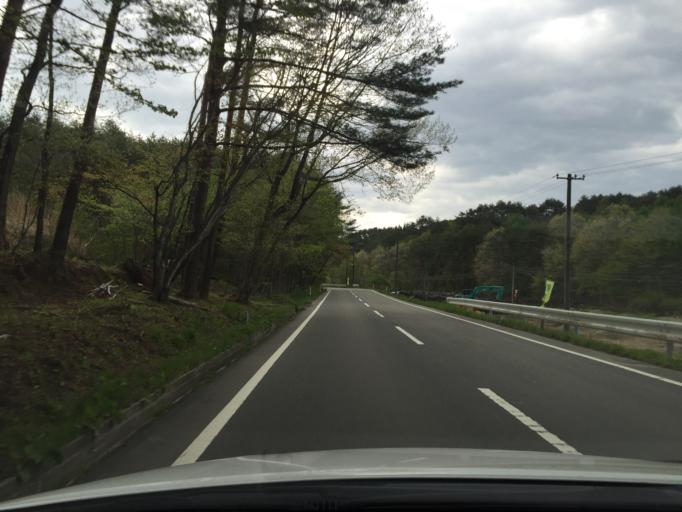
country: JP
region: Fukushima
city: Yanagawamachi-saiwaicho
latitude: 37.7135
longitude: 140.7361
